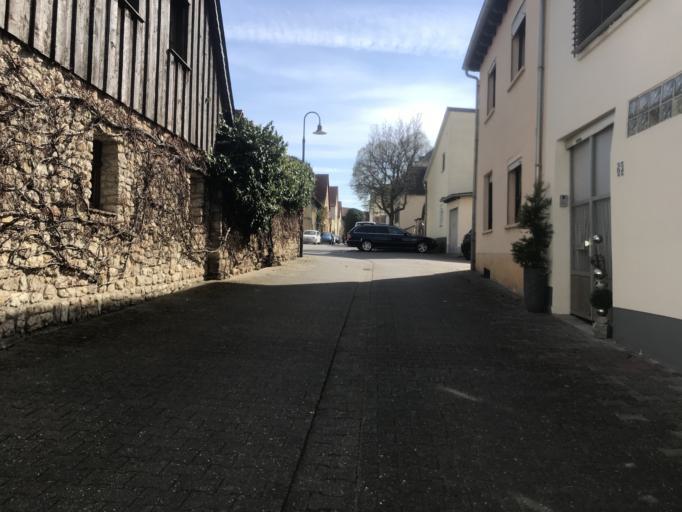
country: DE
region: Rheinland-Pfalz
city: Stadecken-Elsheim
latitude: 49.9135
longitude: 8.1371
